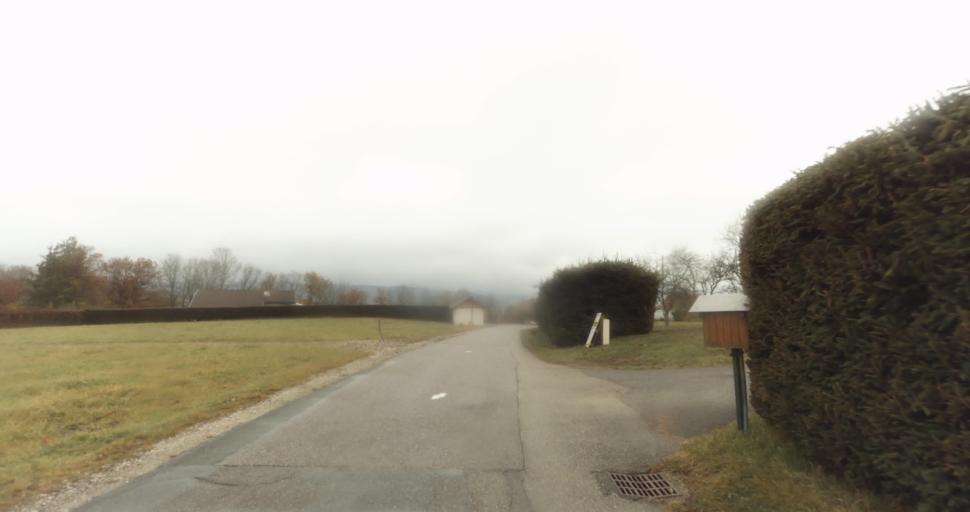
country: FR
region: Rhone-Alpes
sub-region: Departement de la Haute-Savoie
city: Evires
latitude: 46.0601
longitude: 6.2270
